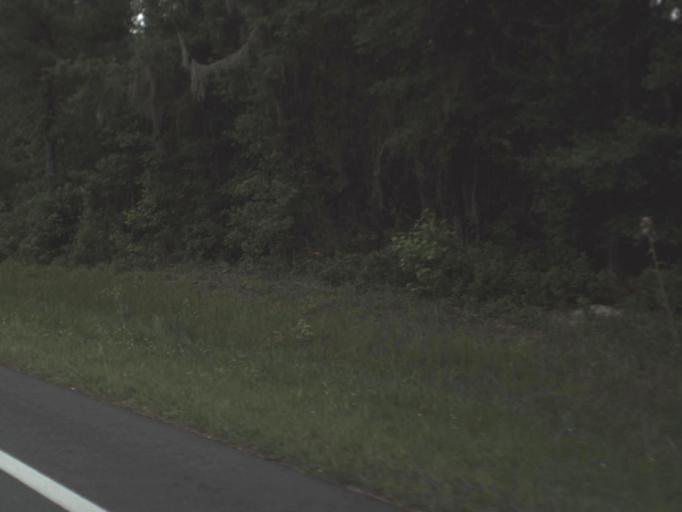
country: US
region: Florida
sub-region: Columbia County
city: Five Points
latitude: 30.4445
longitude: -82.6467
